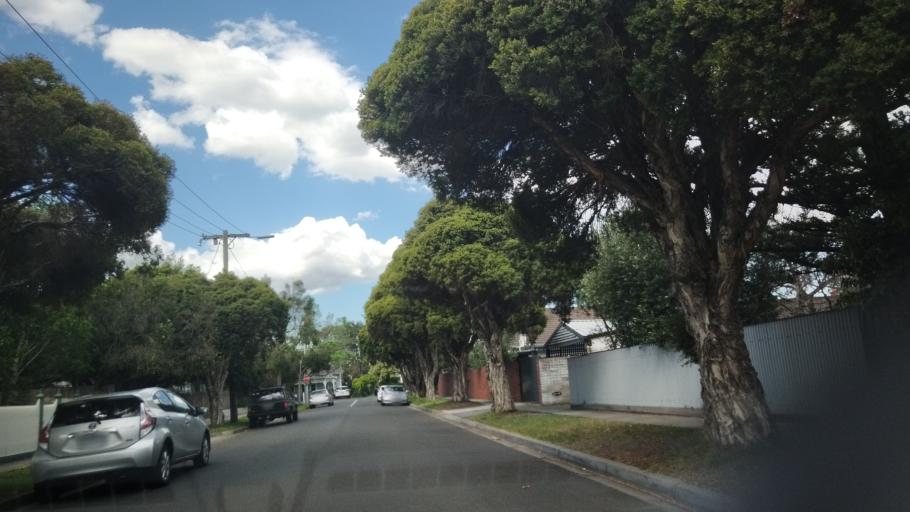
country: AU
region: Victoria
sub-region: Glen Eira
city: Carnegie
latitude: -37.8821
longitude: 145.0575
